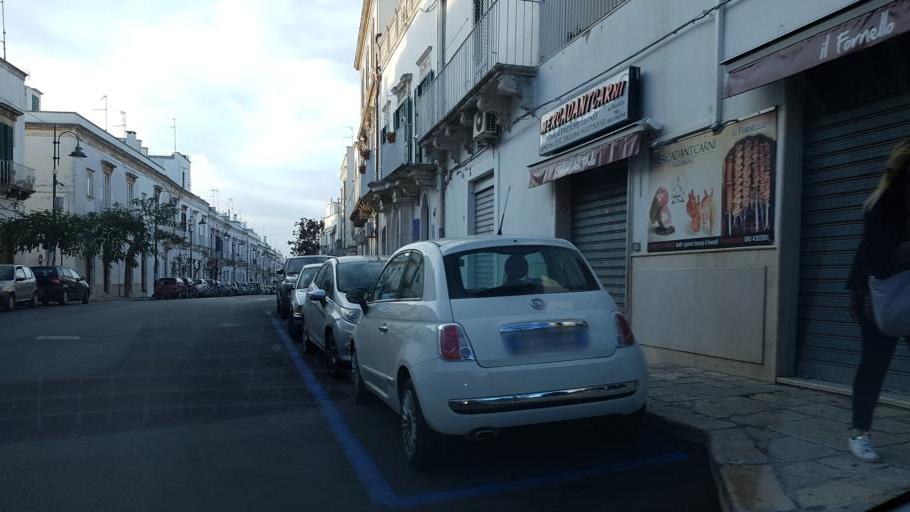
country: IT
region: Apulia
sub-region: Provincia di Taranto
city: Martina Franca
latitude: 40.7032
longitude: 17.3369
